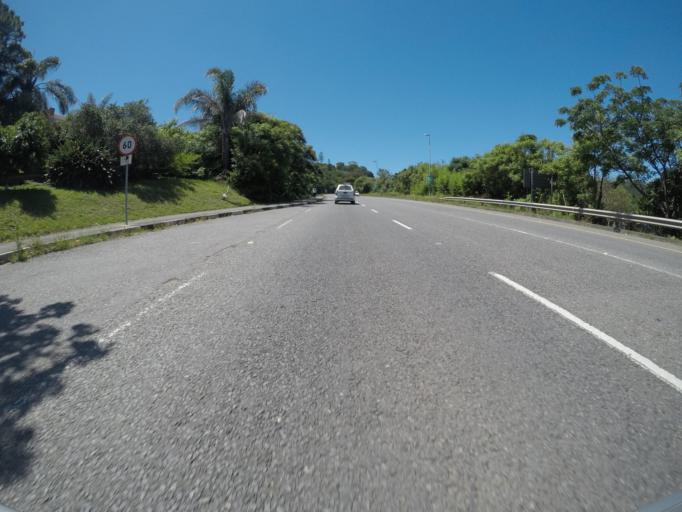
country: ZA
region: Eastern Cape
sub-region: Buffalo City Metropolitan Municipality
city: East London
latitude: -32.9723
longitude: 27.9282
